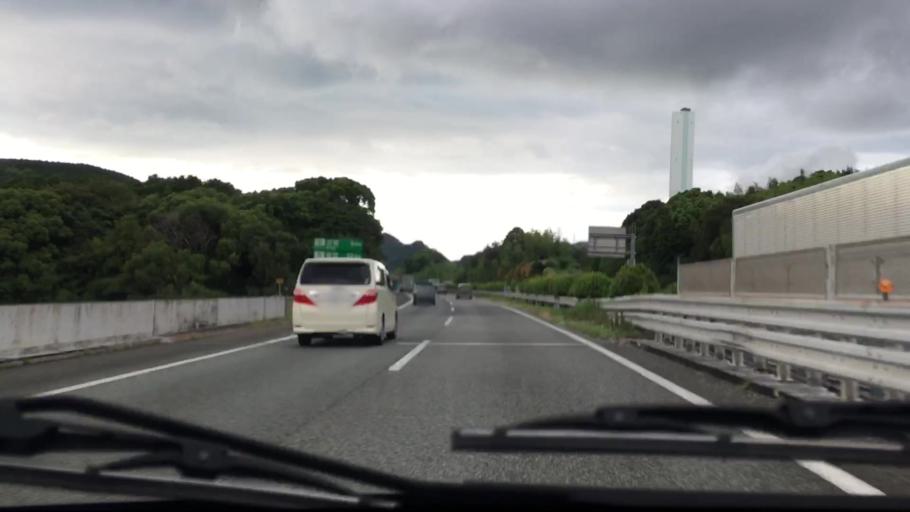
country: JP
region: Fukuoka
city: Sasaguri
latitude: 33.6394
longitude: 130.4889
